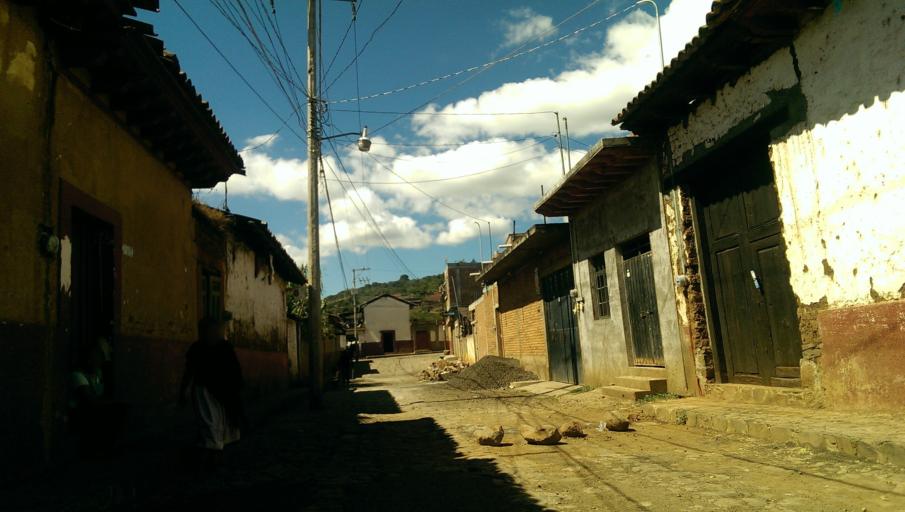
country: MX
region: Michoacan
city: Santa Fe de la Laguna
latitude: 19.6740
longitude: -101.5572
